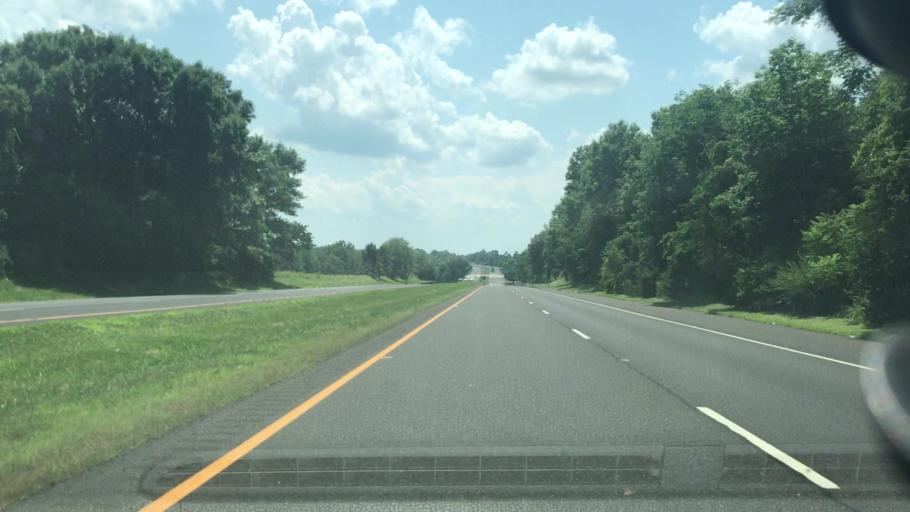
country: US
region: New Jersey
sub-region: Hunterdon County
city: Lambertville
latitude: 40.4072
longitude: -74.9051
